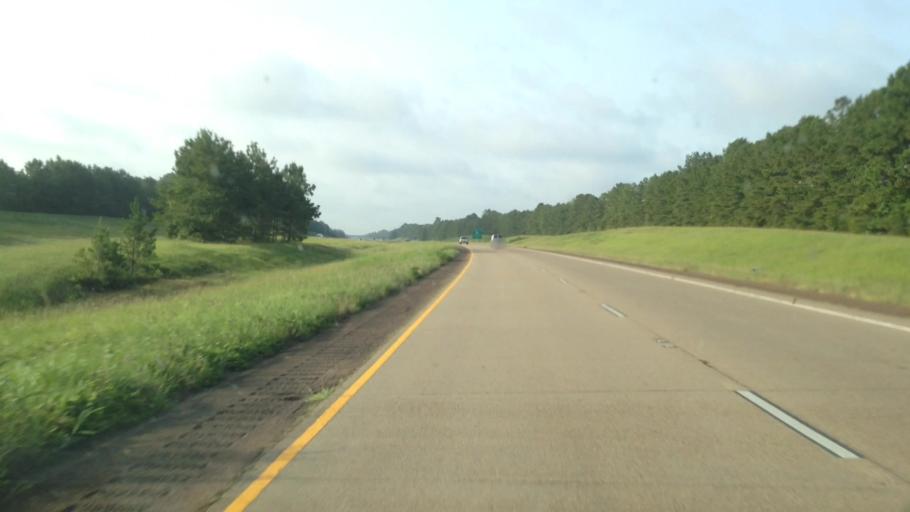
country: US
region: Louisiana
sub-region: Rapides Parish
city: Lecompte
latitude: 31.0914
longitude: -92.4444
